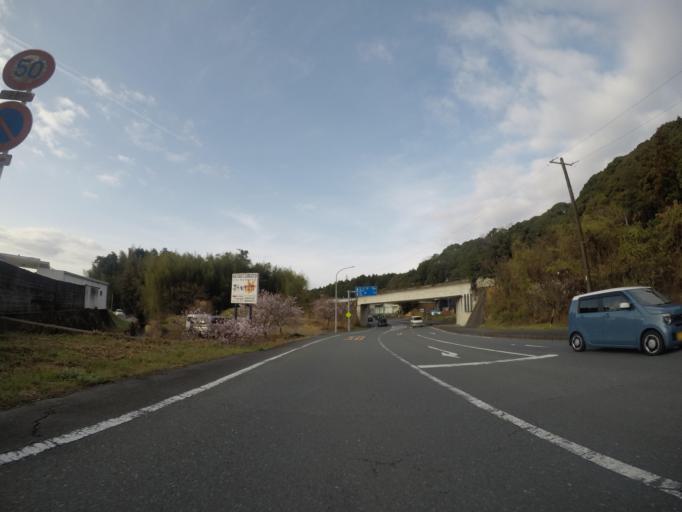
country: JP
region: Shizuoka
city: Hamakita
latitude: 34.8257
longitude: 137.7155
